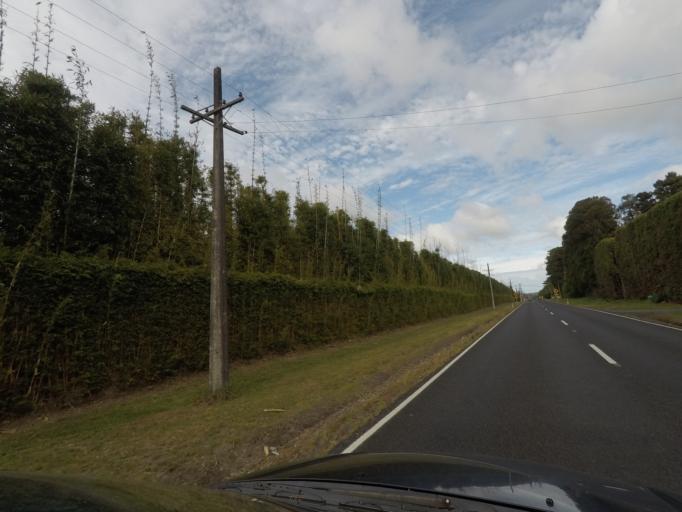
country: NZ
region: Auckland
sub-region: Auckland
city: Rosebank
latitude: -36.7760
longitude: 174.5799
